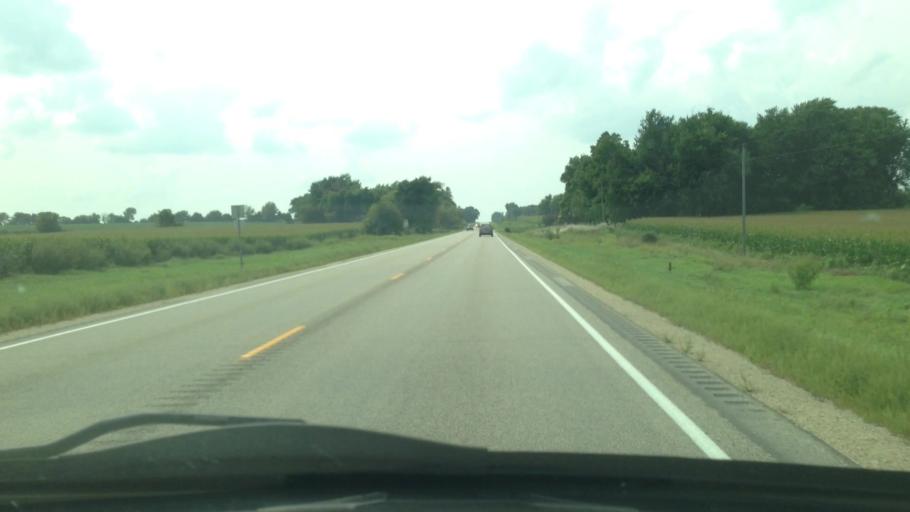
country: US
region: Minnesota
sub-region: Wabasha County
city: Elgin
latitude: 44.1658
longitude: -92.3805
